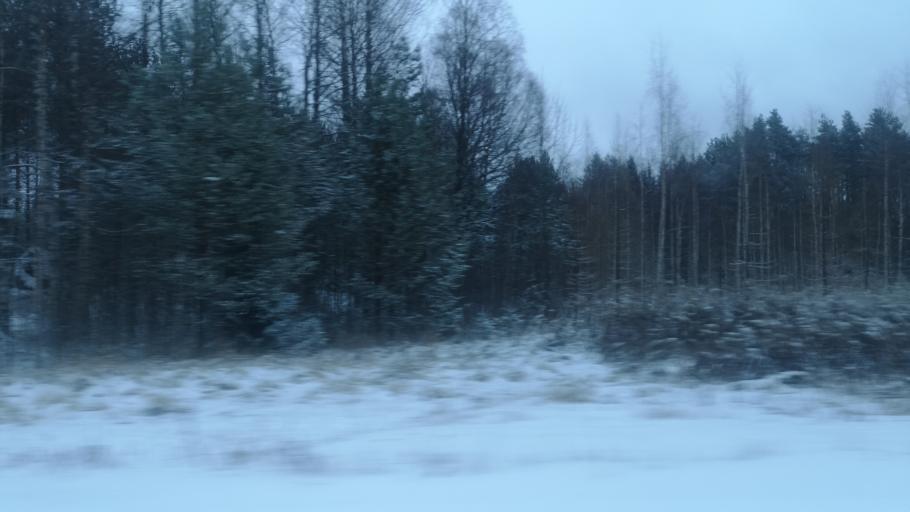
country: FI
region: Southern Savonia
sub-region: Savonlinna
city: Enonkoski
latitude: 62.0453
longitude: 28.7044
